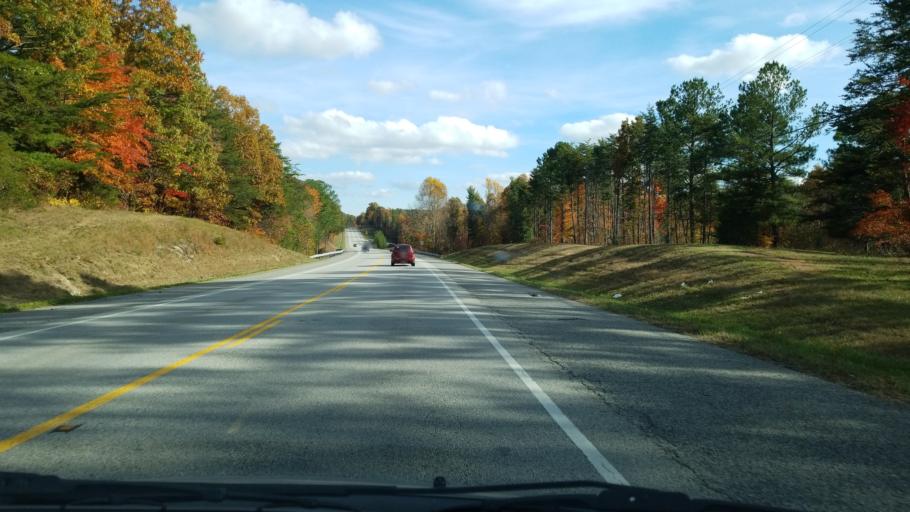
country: US
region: Tennessee
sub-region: Sequatchie County
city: Dunlap
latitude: 35.4431
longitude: -85.4321
